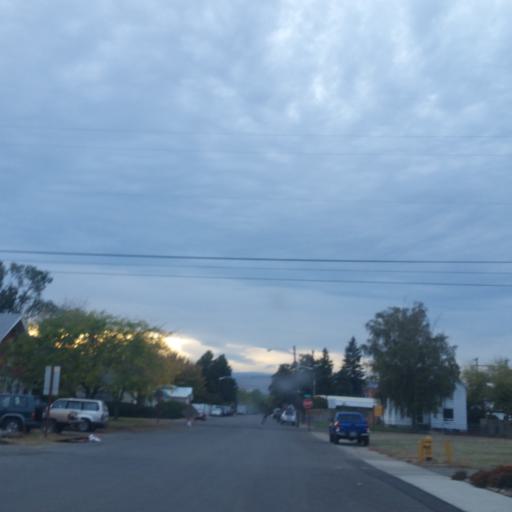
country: US
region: Washington
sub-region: Kittitas County
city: Ellensburg
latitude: 46.9924
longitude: -120.5447
